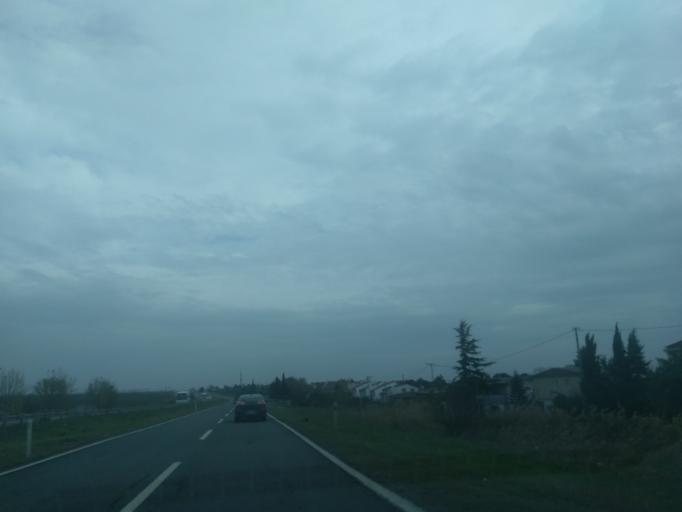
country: TR
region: Istanbul
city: Silivri
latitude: 41.0764
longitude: 28.1685
